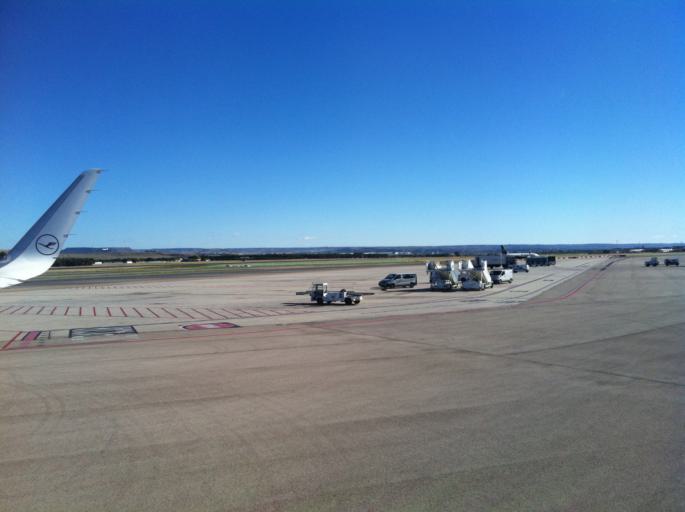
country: ES
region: Madrid
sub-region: Provincia de Madrid
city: Barajas de Madrid
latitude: 40.4723
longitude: -3.5693
